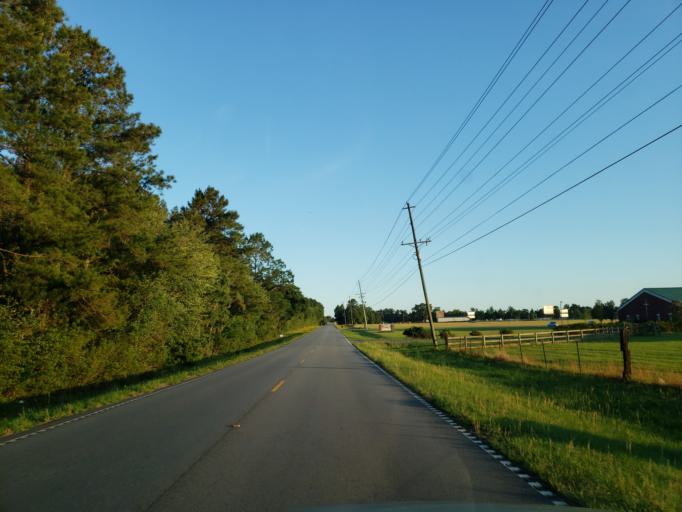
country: US
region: Georgia
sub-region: Lowndes County
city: Valdosta
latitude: 30.7027
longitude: -83.2409
